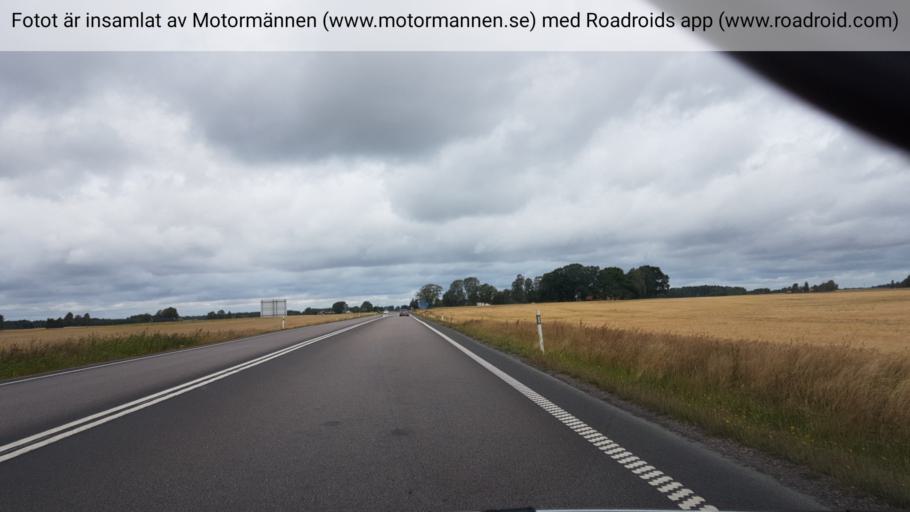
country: SE
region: Vaestra Goetaland
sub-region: Skara Kommun
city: Skara
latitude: 58.4002
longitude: 13.3976
